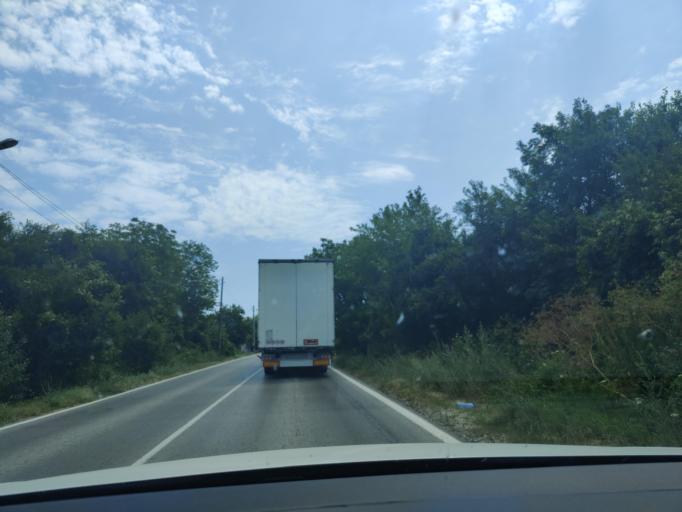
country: BG
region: Vidin
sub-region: Obshtina Ruzhintsi
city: Ruzhintsi
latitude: 43.6511
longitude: 22.7911
